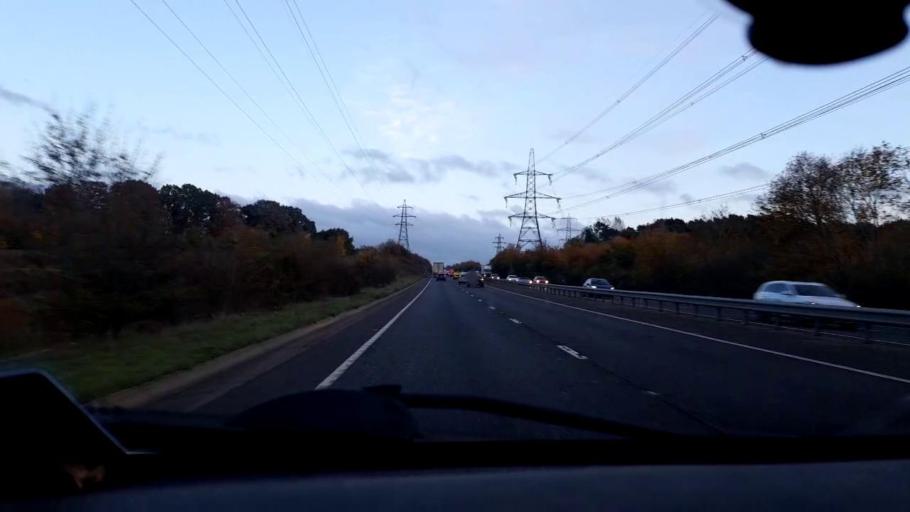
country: GB
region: England
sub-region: Norfolk
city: Cringleford
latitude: 52.5915
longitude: 1.2466
